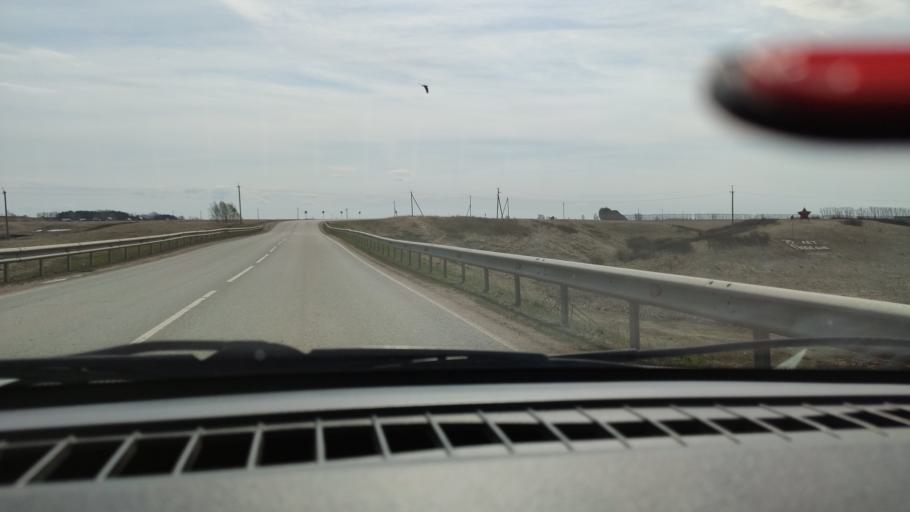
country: RU
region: Bashkortostan
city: Dyurtyuli
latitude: 55.4622
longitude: 54.7961
